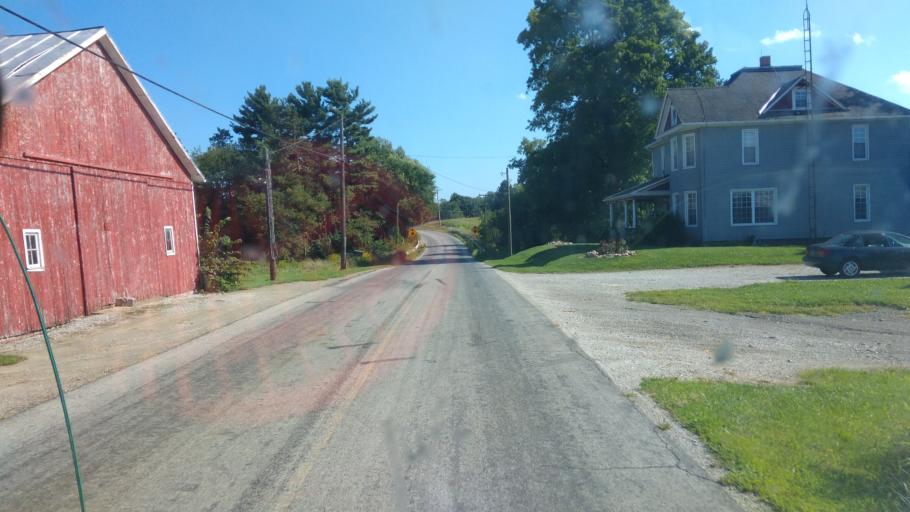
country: US
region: Ohio
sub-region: Ashland County
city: Ashland
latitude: 40.8903
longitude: -82.4277
